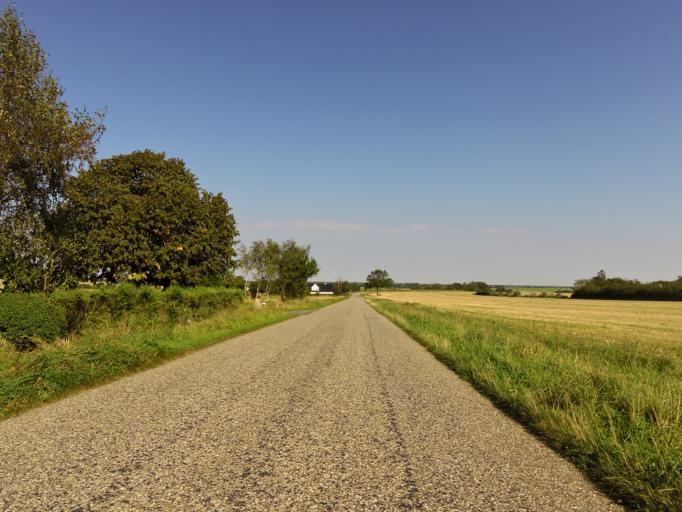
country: DK
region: South Denmark
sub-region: Vejen Kommune
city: Rodding
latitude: 55.3295
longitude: 9.1193
